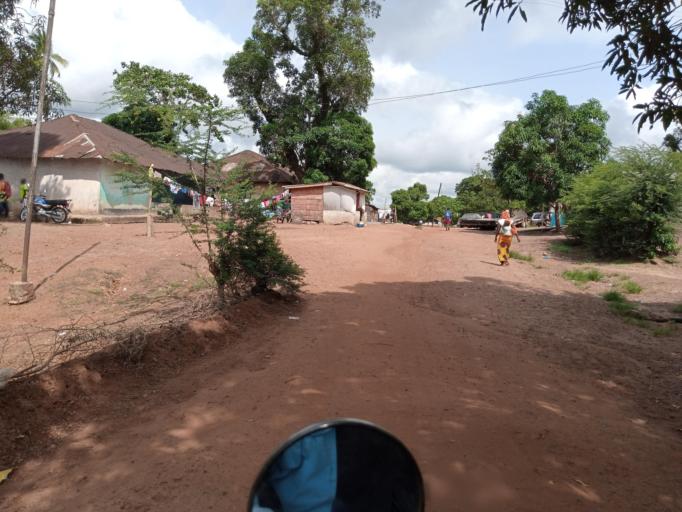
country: SL
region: Southern Province
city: Bo
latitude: 7.9614
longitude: -11.7362
